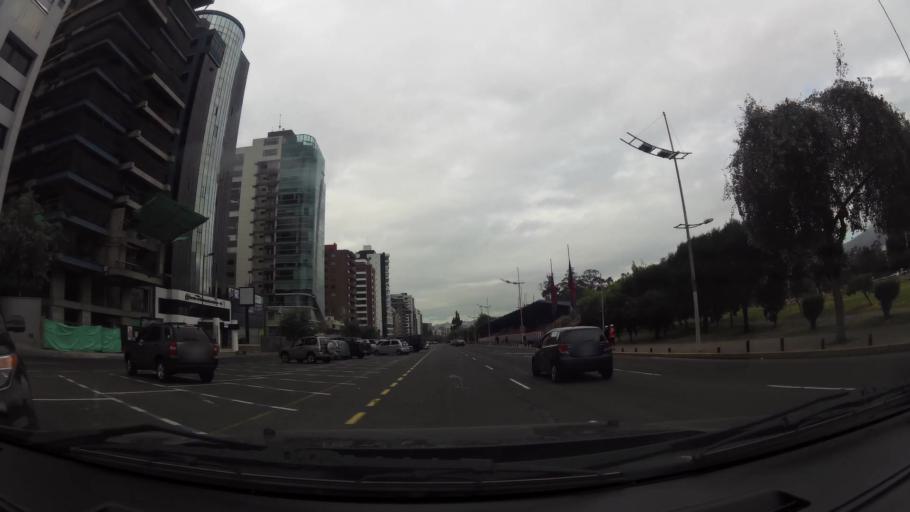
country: EC
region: Pichincha
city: Quito
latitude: -0.1819
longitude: -78.4820
